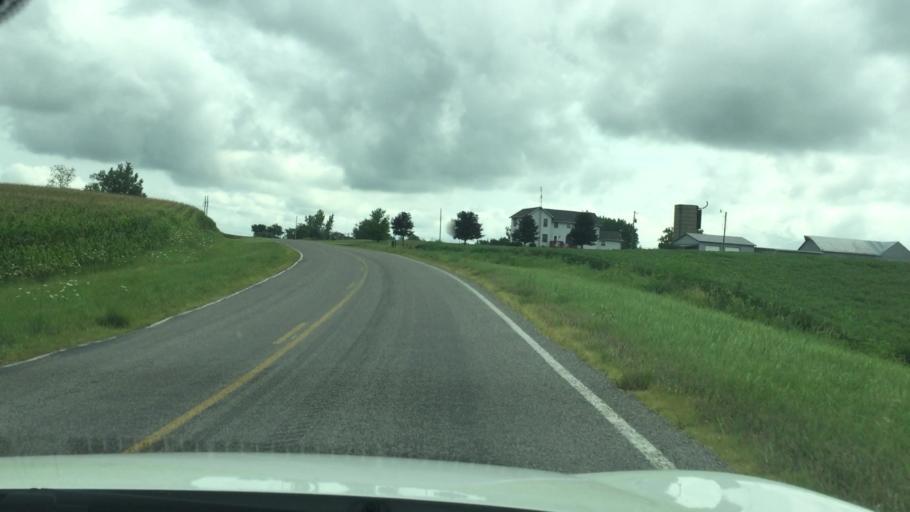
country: US
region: Ohio
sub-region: Champaign County
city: Mechanicsburg
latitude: 40.0596
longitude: -83.6547
